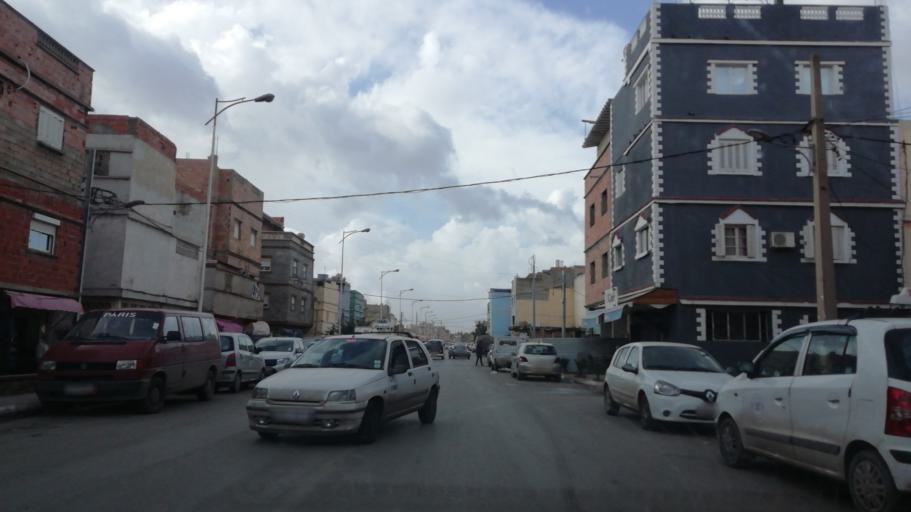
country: DZ
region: Oran
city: Oran
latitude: 35.6825
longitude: -0.6164
